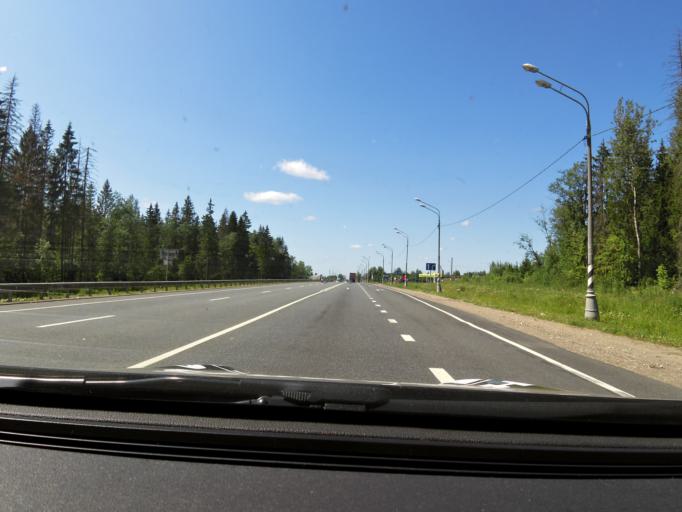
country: RU
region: Novgorod
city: Kresttsy
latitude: 58.2423
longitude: 32.5604
